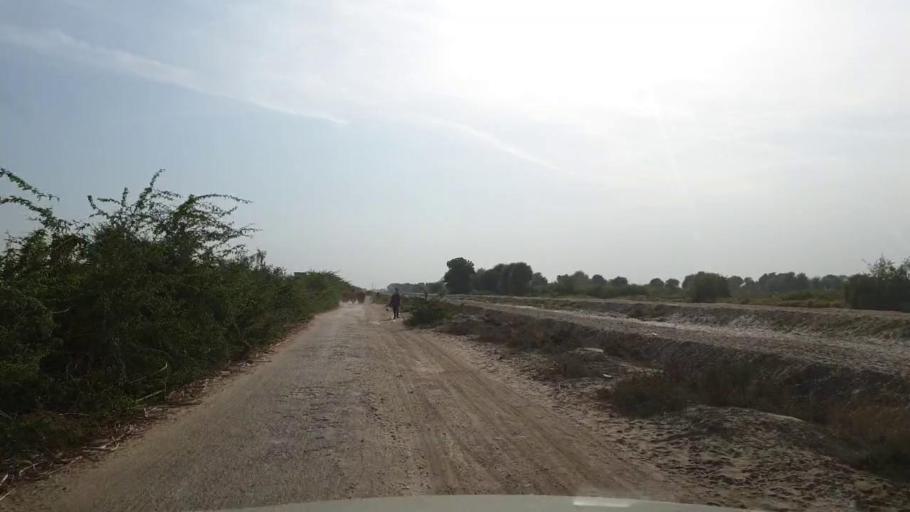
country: PK
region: Sindh
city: Kunri
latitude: 25.1677
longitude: 69.5243
